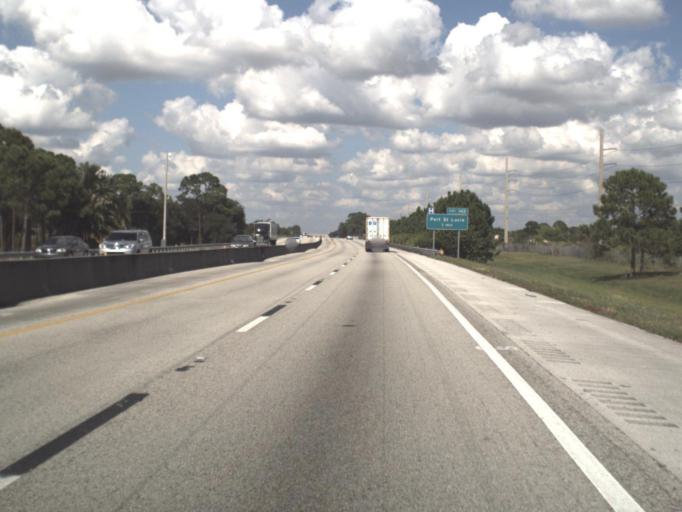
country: US
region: Florida
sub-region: Saint Lucie County
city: Port Saint Lucie
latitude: 27.2591
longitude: -80.3504
